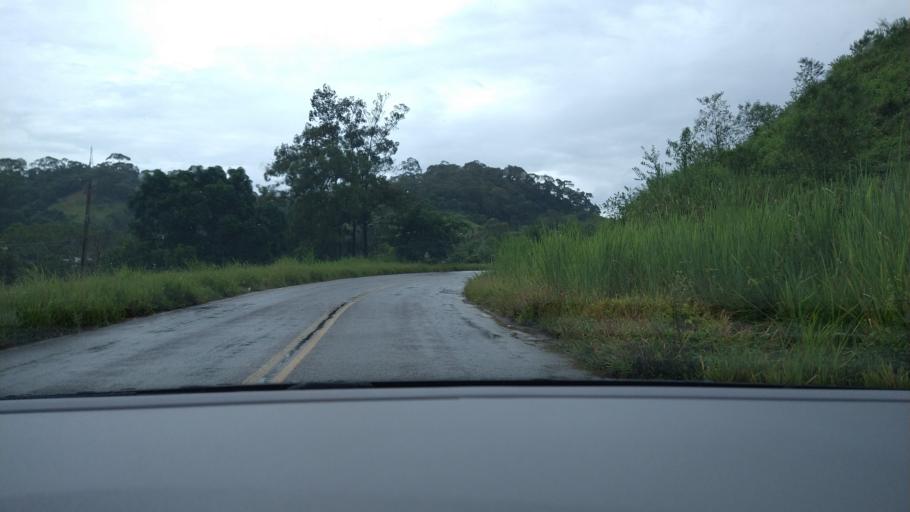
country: BR
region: Minas Gerais
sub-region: Ponte Nova
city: Ponte Nova
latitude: -20.3793
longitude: -42.9017
